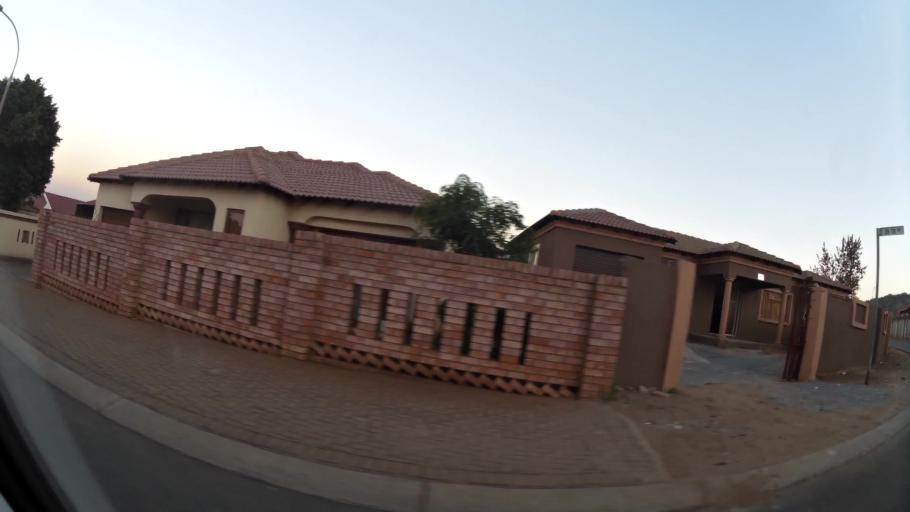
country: ZA
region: North-West
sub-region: Bojanala Platinum District Municipality
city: Rustenburg
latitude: -25.6548
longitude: 27.2051
